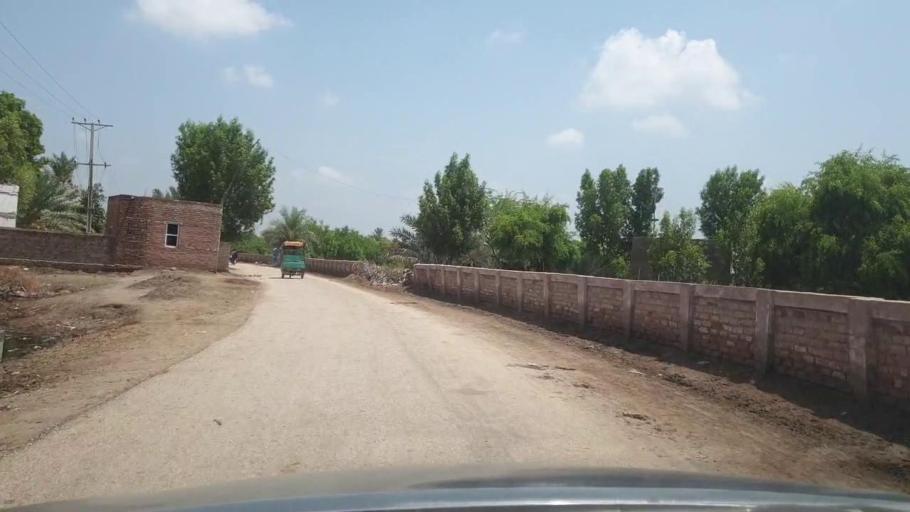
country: PK
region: Sindh
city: Pir jo Goth
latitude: 27.5982
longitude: 68.6064
